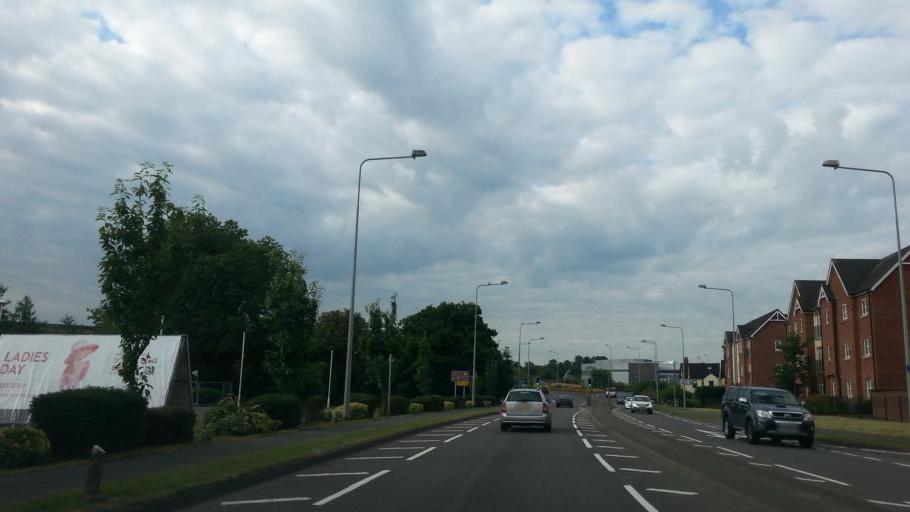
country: GB
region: England
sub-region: Staffordshire
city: Uttoxeter
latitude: 52.8989
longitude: -1.8603
